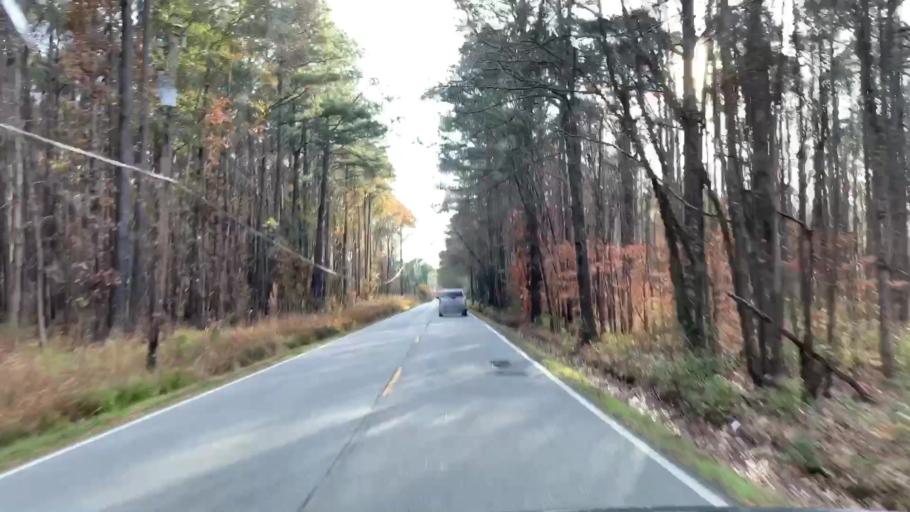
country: US
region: Virginia
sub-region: City of Virginia Beach
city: Virginia Beach
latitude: 36.7390
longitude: -76.1073
